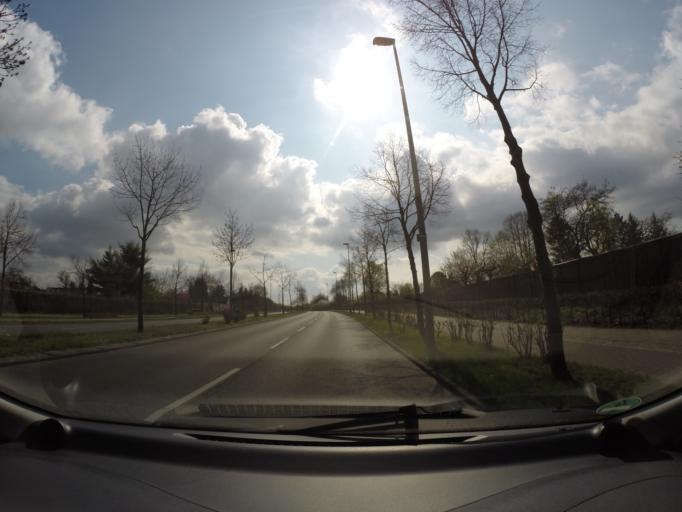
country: DE
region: Berlin
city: Kaulsdorf
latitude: 52.5347
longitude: 13.5858
